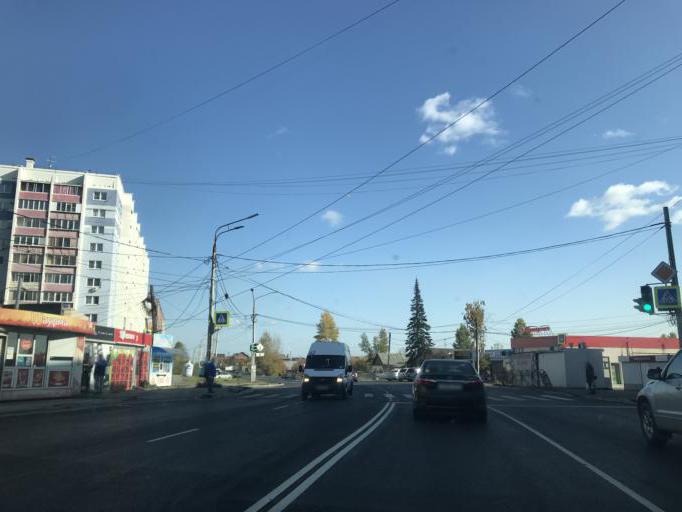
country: RU
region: Chelyabinsk
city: Roshchino
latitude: 55.2348
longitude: 61.3000
